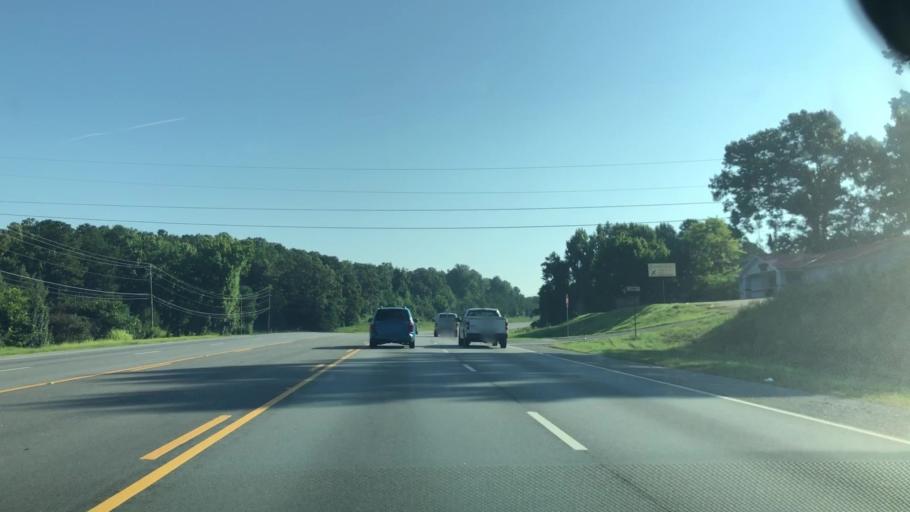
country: US
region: Alabama
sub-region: Calhoun County
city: West End-Cobb Town
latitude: 33.6316
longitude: -85.9143
